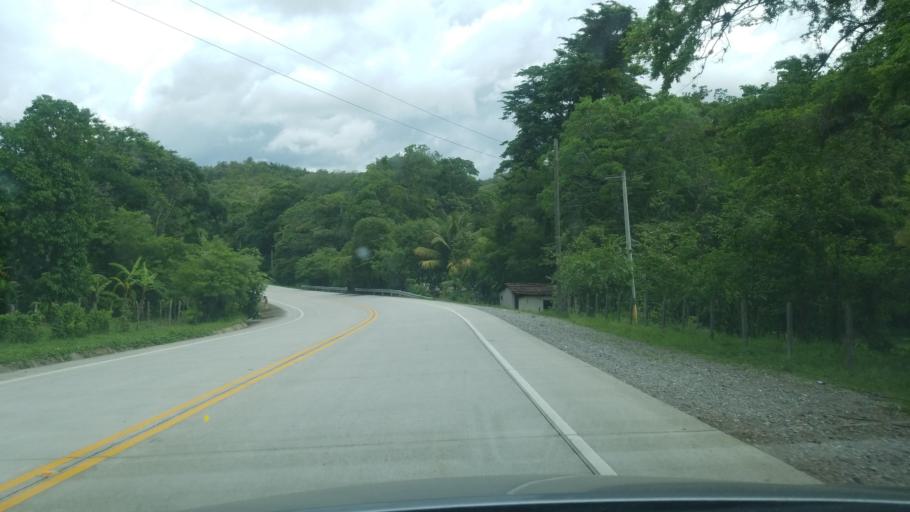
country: HN
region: Copan
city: Florida
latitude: 15.0026
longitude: -88.8379
